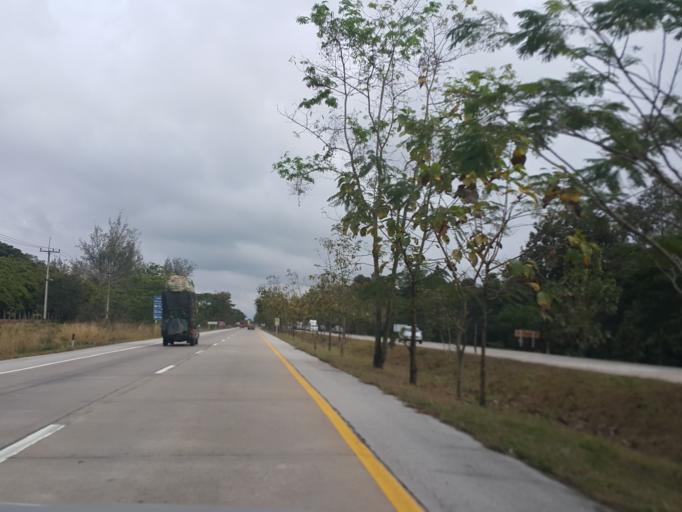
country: TH
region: Lampang
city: Hang Chat
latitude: 18.3233
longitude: 99.2958
